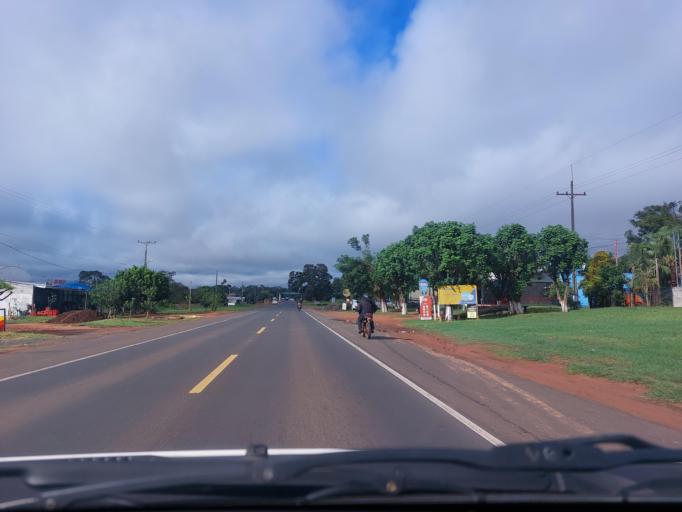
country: PY
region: San Pedro
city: Guayaybi
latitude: -24.5778
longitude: -56.4024
